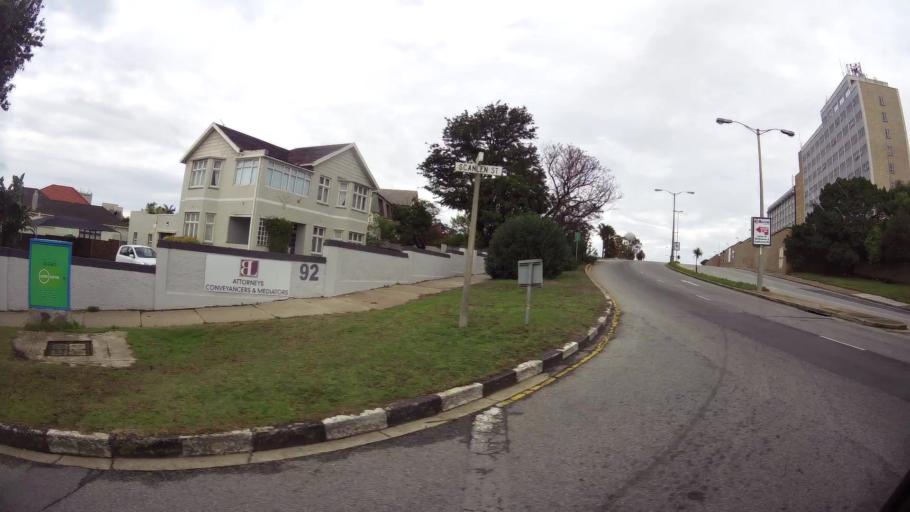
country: ZA
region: Eastern Cape
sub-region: Nelson Mandela Bay Metropolitan Municipality
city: Port Elizabeth
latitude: -33.9546
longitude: 25.5966
